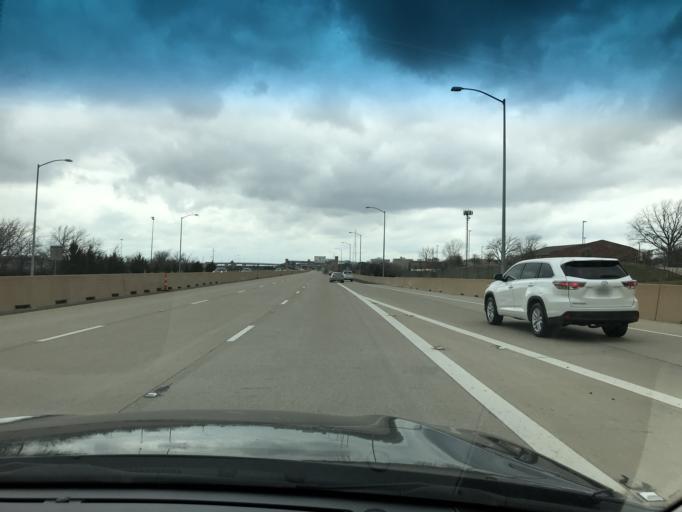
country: US
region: Texas
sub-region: Tarrant County
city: Westworth
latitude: 32.7283
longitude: -97.3727
